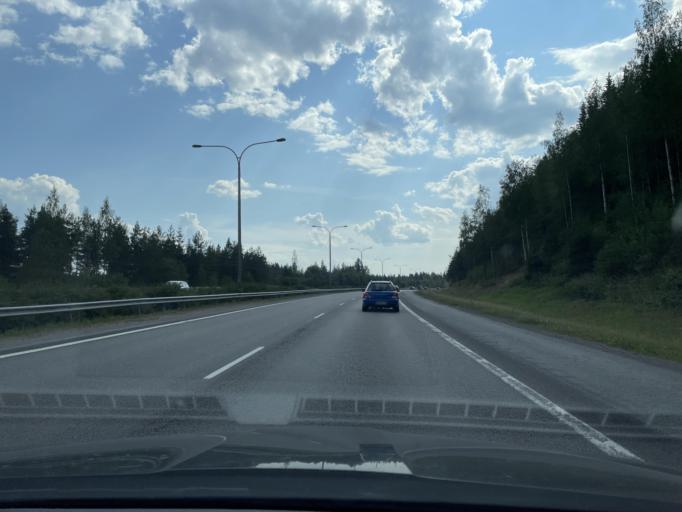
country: FI
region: Central Finland
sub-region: Jyvaeskylae
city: Jyvaeskylae
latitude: 62.1989
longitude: 25.7089
